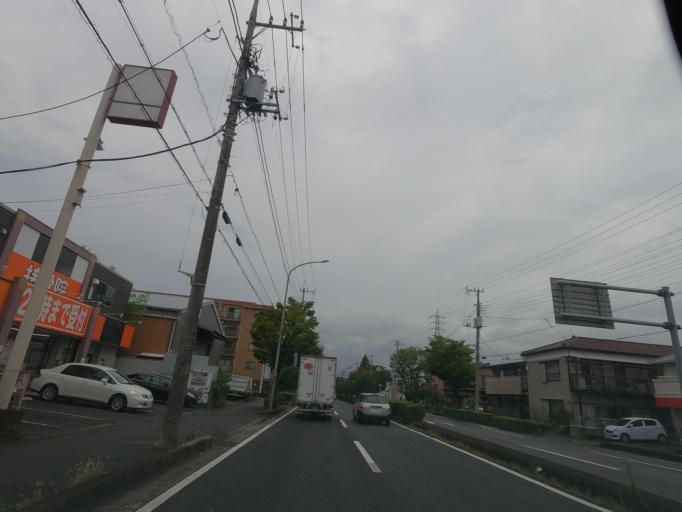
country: JP
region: Saitama
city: Shimotoda
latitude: 35.8521
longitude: 139.7032
